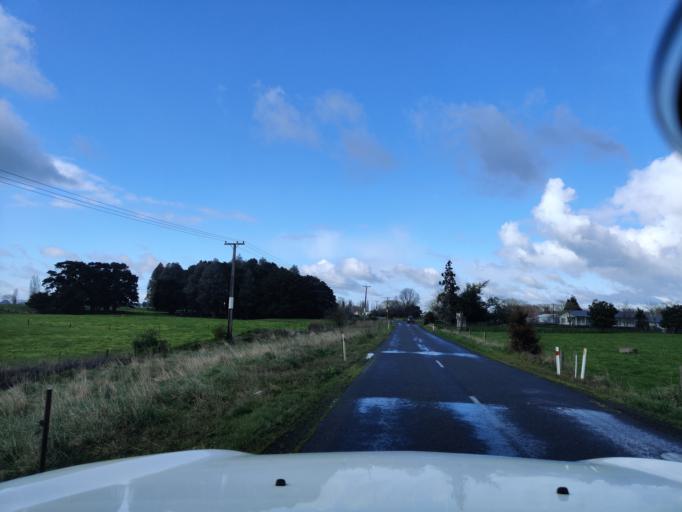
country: NZ
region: Waikato
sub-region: Waikato District
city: Ngaruawahia
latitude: -37.5688
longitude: 175.2635
